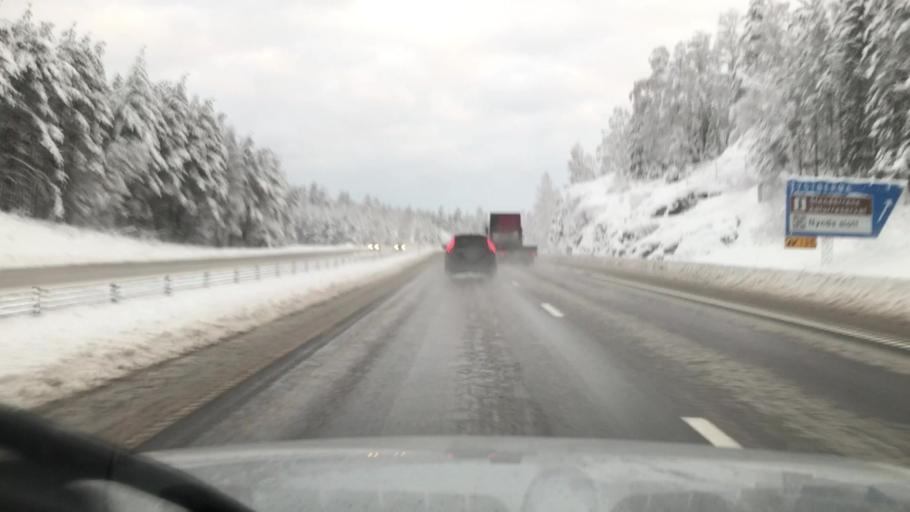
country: SE
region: Soedermanland
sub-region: Oxelosunds Kommun
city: Oxelosund
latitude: 58.8545
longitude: 17.2069
